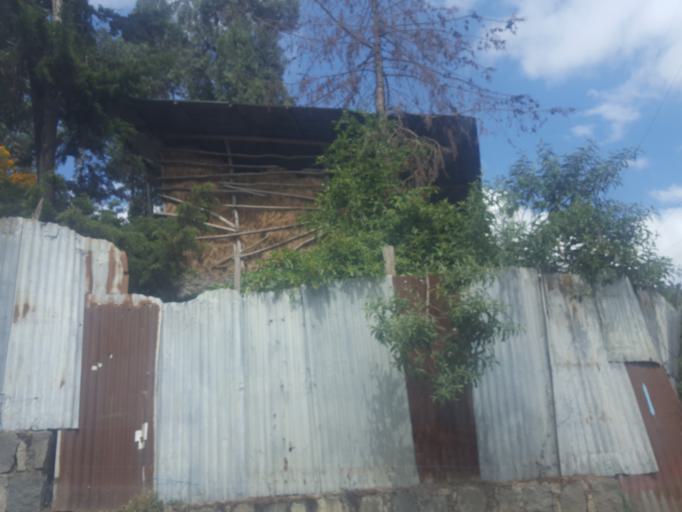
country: ET
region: Adis Abeba
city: Addis Ababa
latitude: 9.0651
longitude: 38.7448
